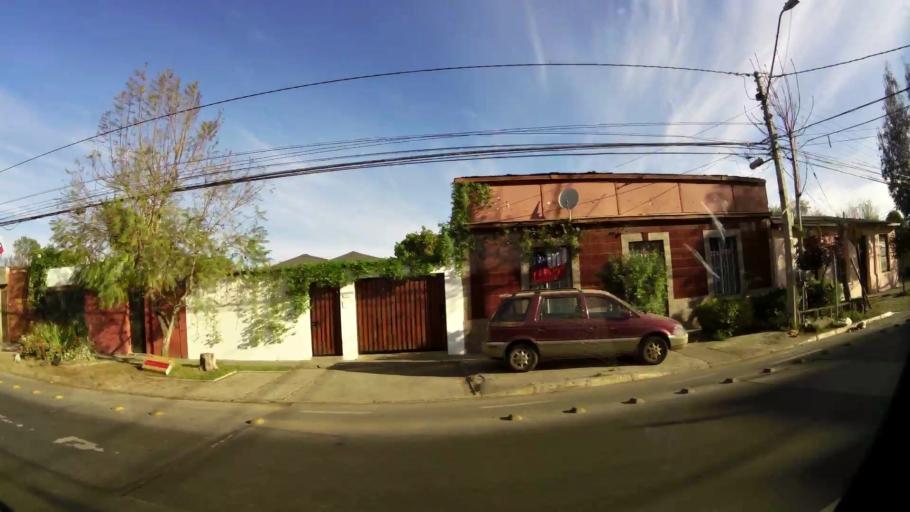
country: CL
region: Santiago Metropolitan
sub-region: Provincia de Santiago
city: Lo Prado
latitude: -33.4354
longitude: -70.6949
